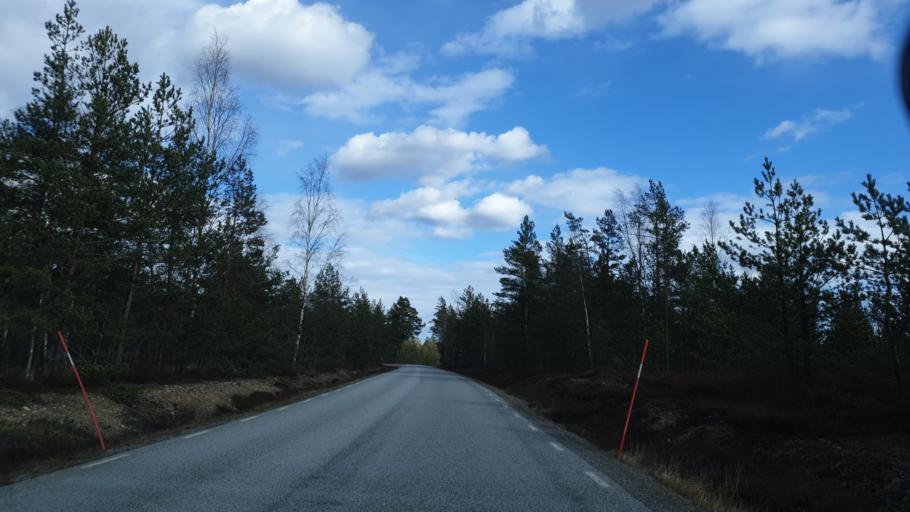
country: SE
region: Stockholm
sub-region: Varmdo Kommun
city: Mortnas
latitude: 59.2570
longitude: 18.4377
